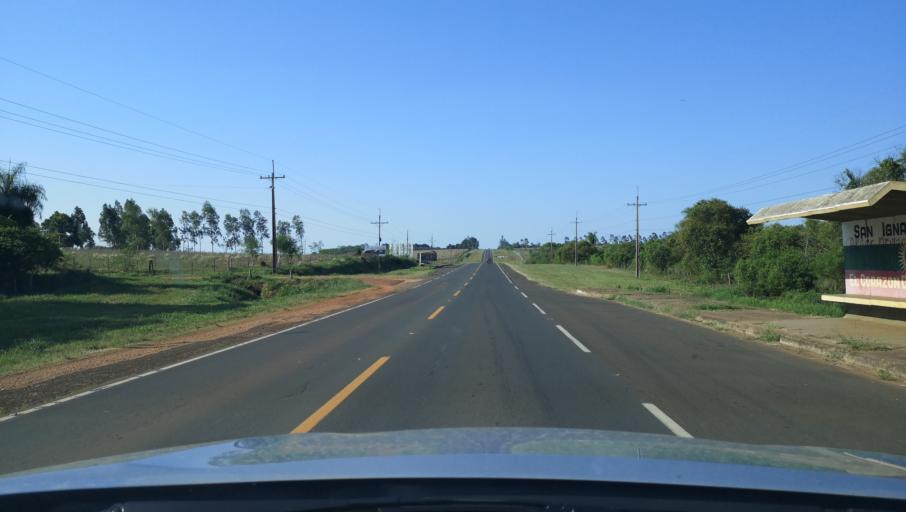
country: PY
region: Misiones
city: Santa Maria
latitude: -26.8336
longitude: -57.0326
